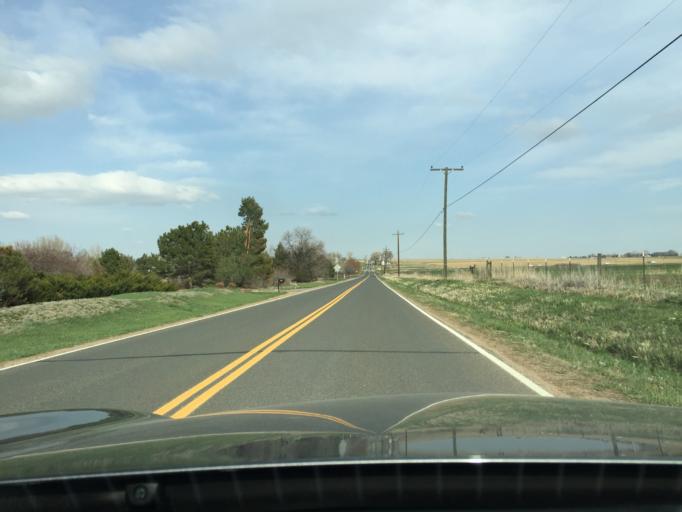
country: US
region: Colorado
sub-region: Boulder County
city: Longmont
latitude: 40.1162
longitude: -105.1096
